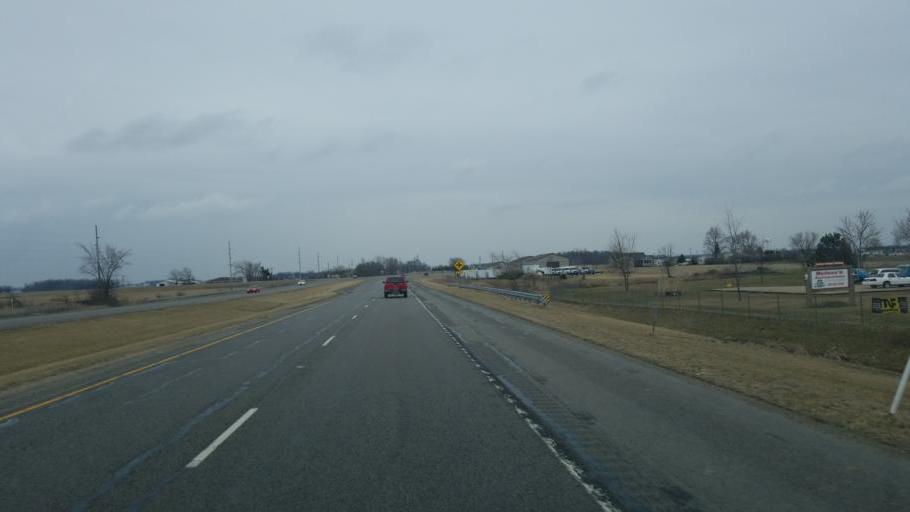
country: US
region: Indiana
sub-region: Adams County
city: Decatur
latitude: 40.7629
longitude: -84.9378
